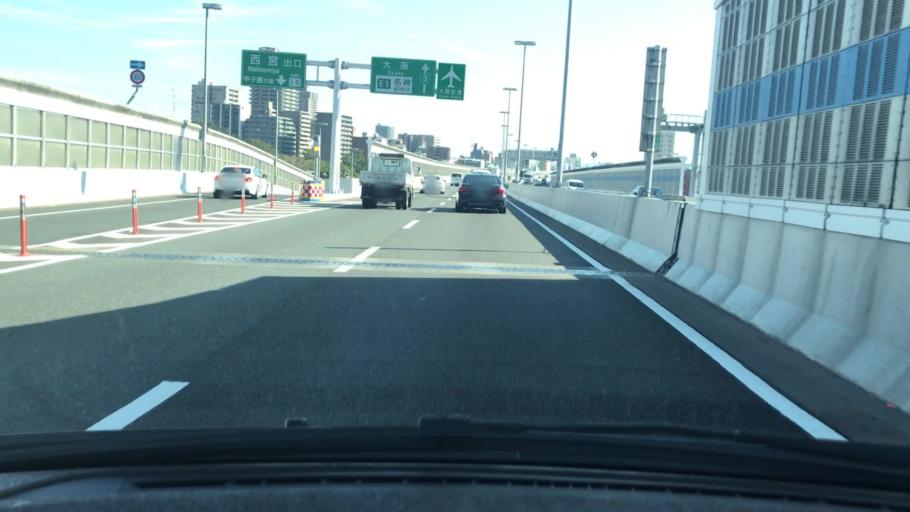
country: JP
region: Hyogo
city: Nishinomiya-hama
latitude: 34.7338
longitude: 135.3307
